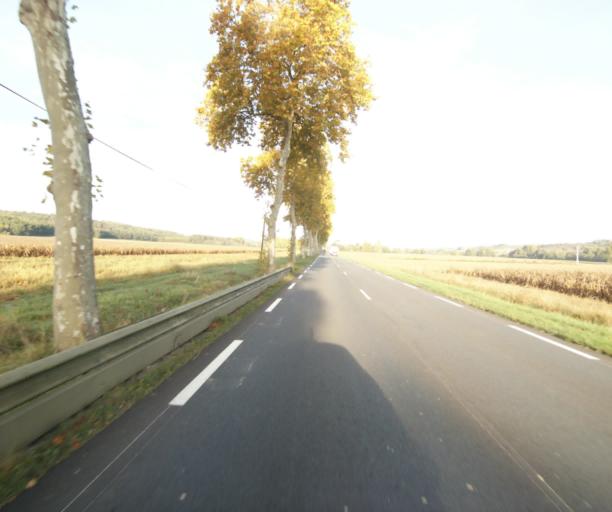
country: FR
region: Midi-Pyrenees
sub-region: Departement du Tarn-et-Garonne
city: Saint-Nauphary
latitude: 43.9416
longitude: 1.4696
